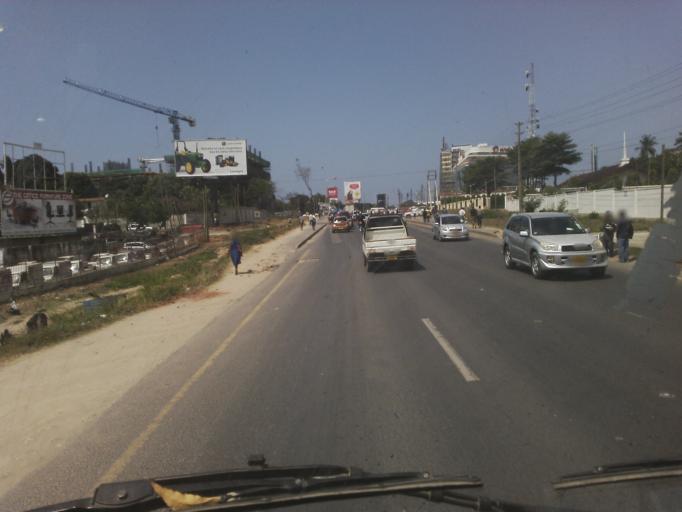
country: TZ
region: Dar es Salaam
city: Magomeni
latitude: -6.7775
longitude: 39.2615
